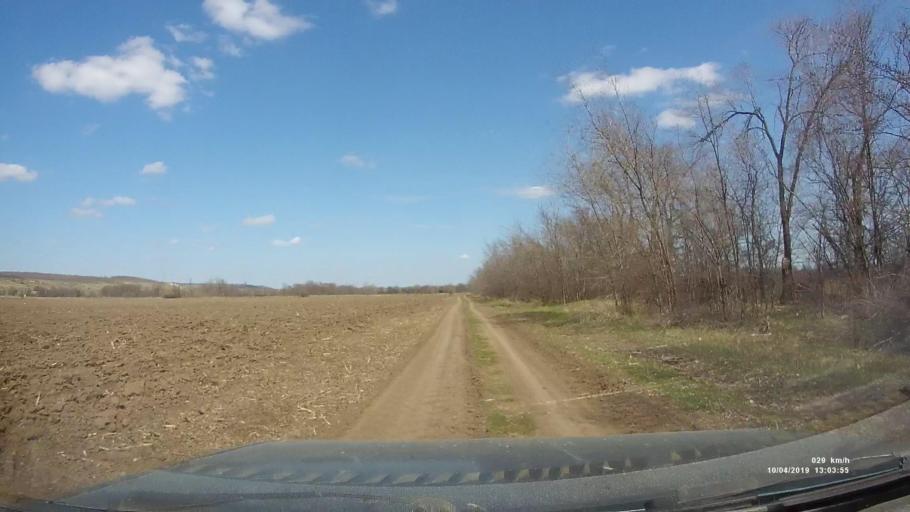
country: RU
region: Rostov
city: Masalovka
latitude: 48.3838
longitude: 40.2346
